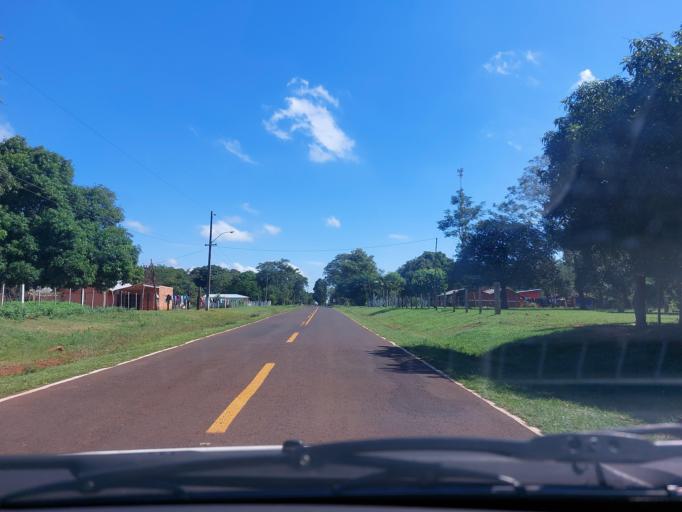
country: PY
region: San Pedro
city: Guayaybi
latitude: -24.5315
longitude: -56.5490
